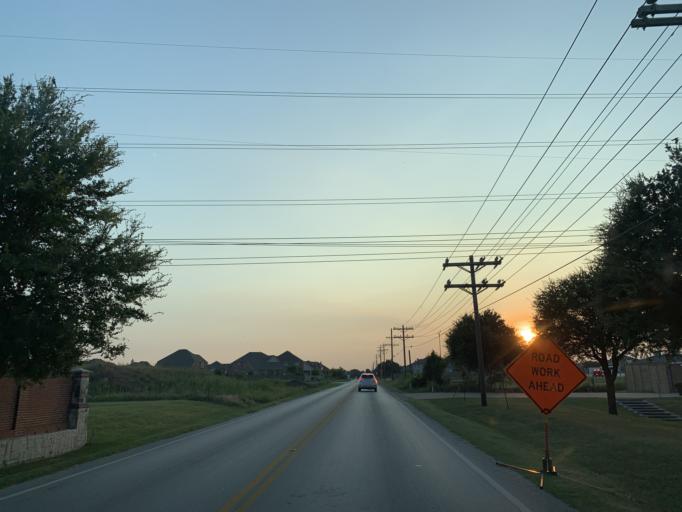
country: US
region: Texas
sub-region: Tarrant County
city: Keller
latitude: 32.9637
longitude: -97.2629
